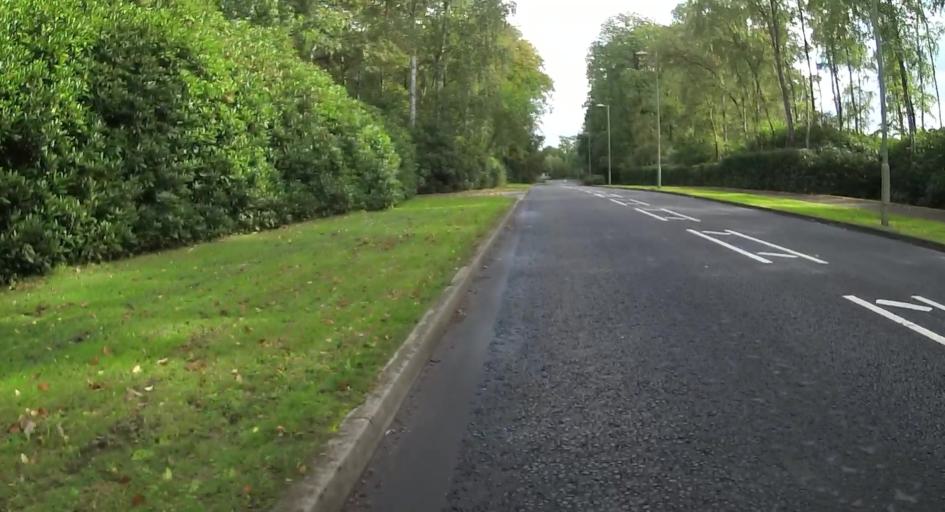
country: GB
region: England
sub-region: Hampshire
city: Fleet
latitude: 51.2978
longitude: -0.8356
